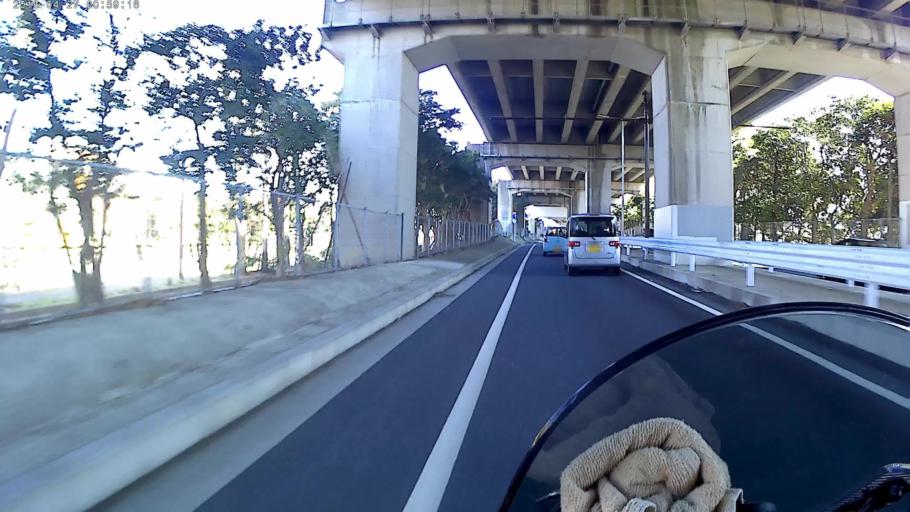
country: JP
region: Kanagawa
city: Chigasaki
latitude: 35.3502
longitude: 139.4124
